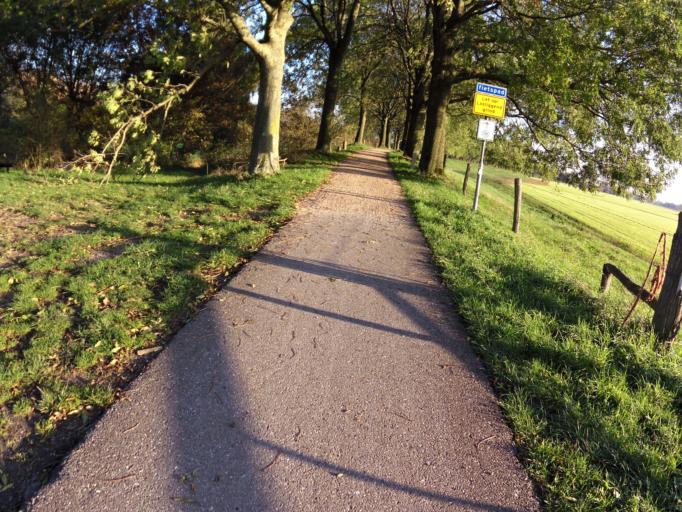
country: NL
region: North Brabant
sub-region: Gemeente Heusden
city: Heusden
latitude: 51.7130
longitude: 5.1026
